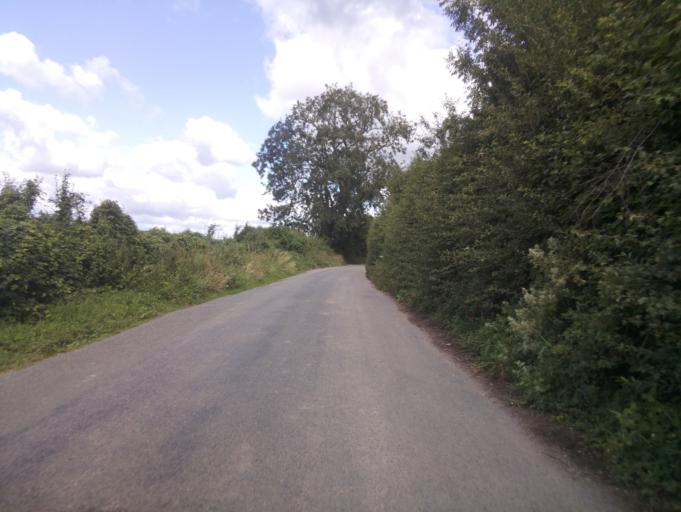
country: GB
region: England
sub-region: Gloucestershire
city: Newent
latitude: 51.8490
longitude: -2.3490
